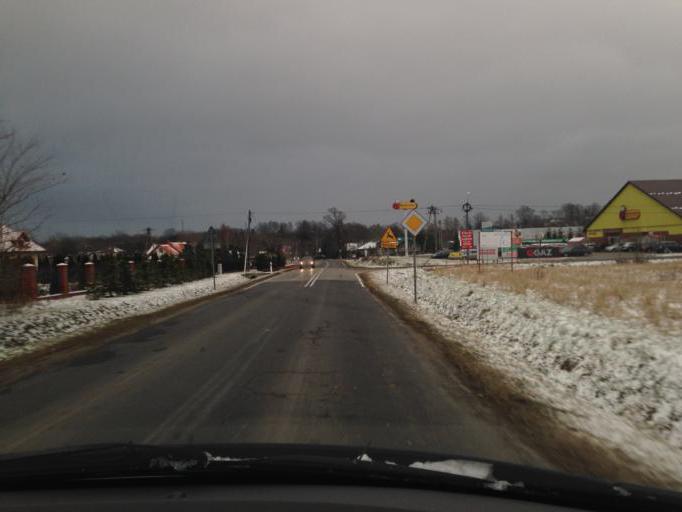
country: PL
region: Subcarpathian Voivodeship
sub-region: Powiat jasielski
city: Nowy Zmigrod
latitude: 49.6085
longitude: 21.5169
